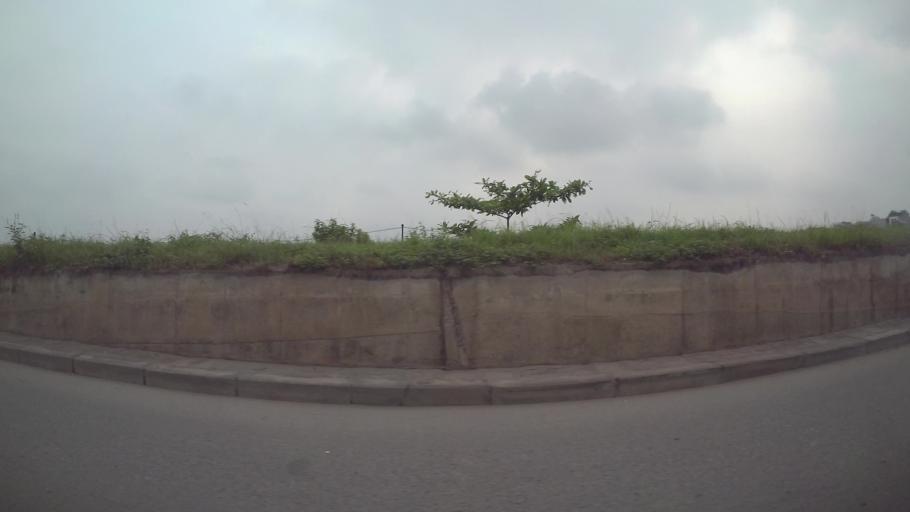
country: VN
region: Ha Noi
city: Trau Quy
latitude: 21.0749
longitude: 105.9144
